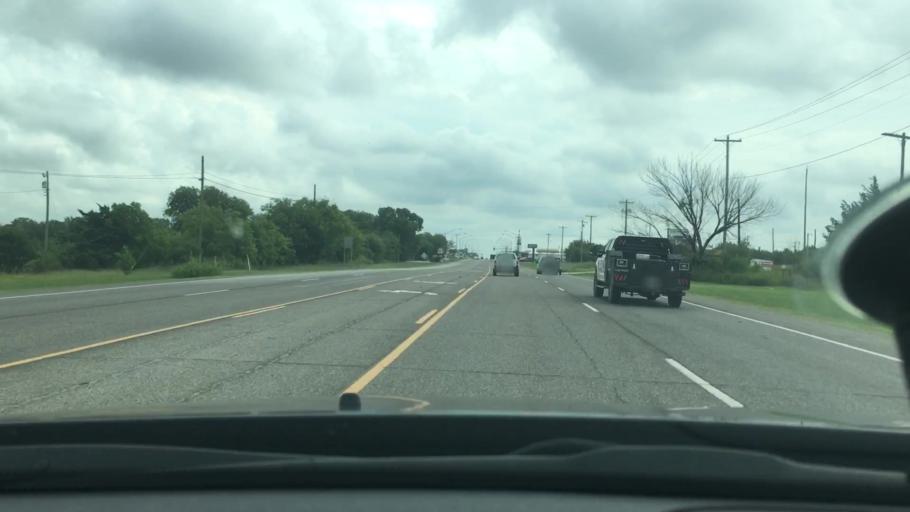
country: US
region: Oklahoma
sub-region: Carter County
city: Lone Grove
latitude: 34.1730
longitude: -97.2695
